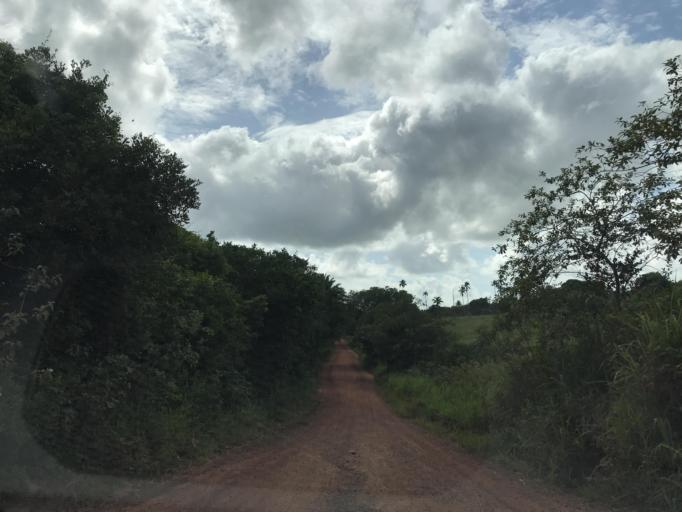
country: BR
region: Bahia
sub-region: Entre Rios
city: Entre Rios
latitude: -12.1746
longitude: -38.1314
